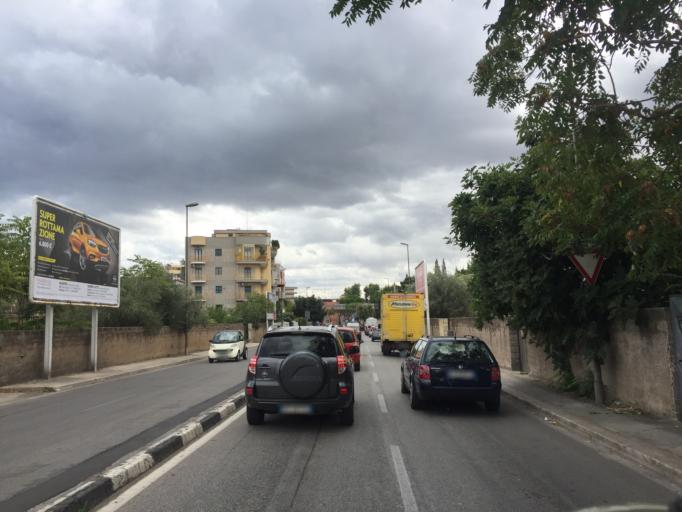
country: IT
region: Apulia
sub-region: Provincia di Bari
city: Bari
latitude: 41.1082
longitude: 16.8573
